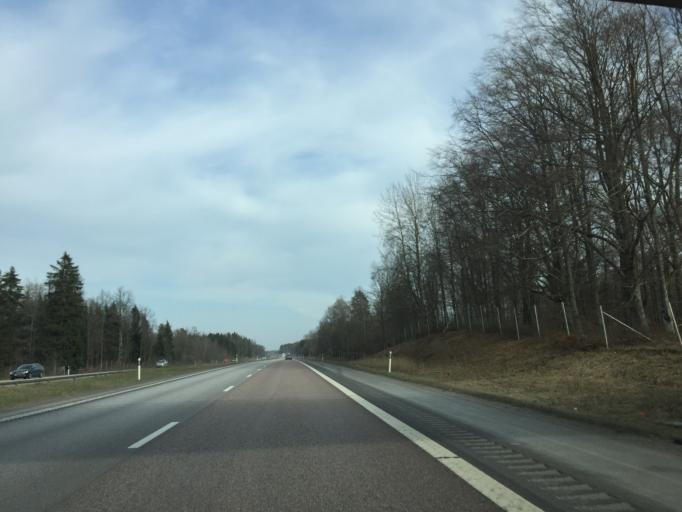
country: SE
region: OErebro
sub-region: Orebro Kommun
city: Hovsta
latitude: 59.3072
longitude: 15.2960
